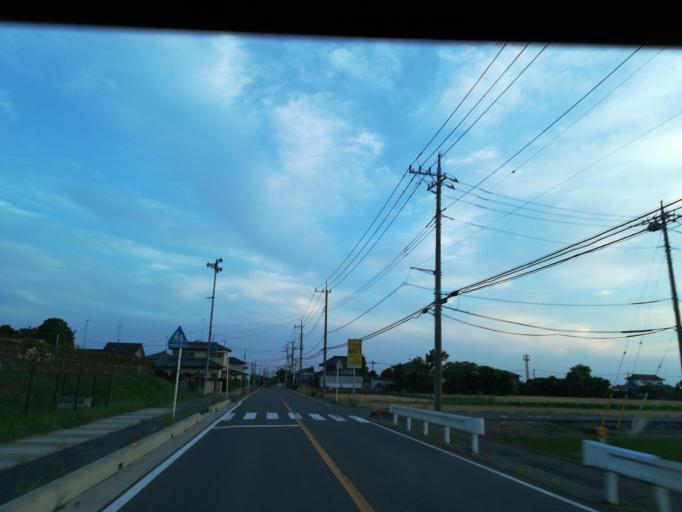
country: JP
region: Saitama
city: Kazo
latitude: 36.1438
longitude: 139.6142
